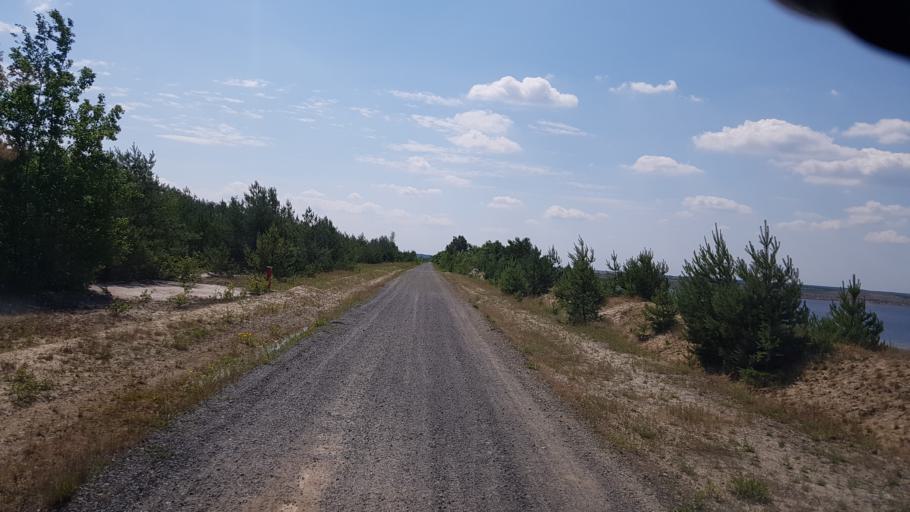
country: DE
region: Brandenburg
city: Sallgast
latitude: 51.5798
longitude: 13.8005
